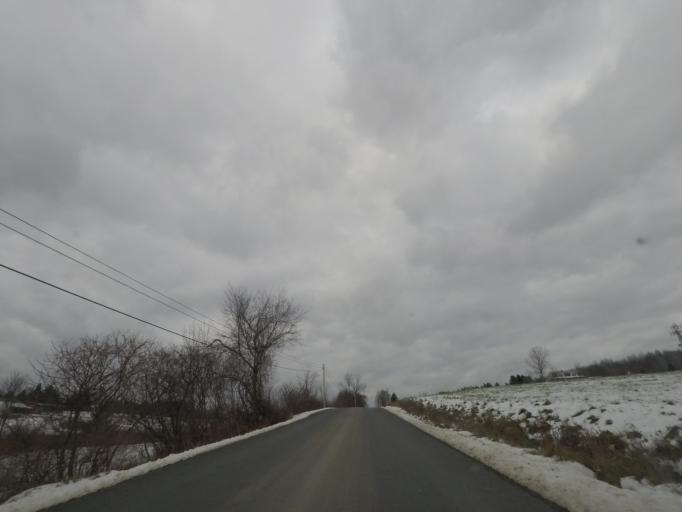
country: US
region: New York
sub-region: Rensselaer County
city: West Sand Lake
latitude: 42.5929
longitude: -73.6305
